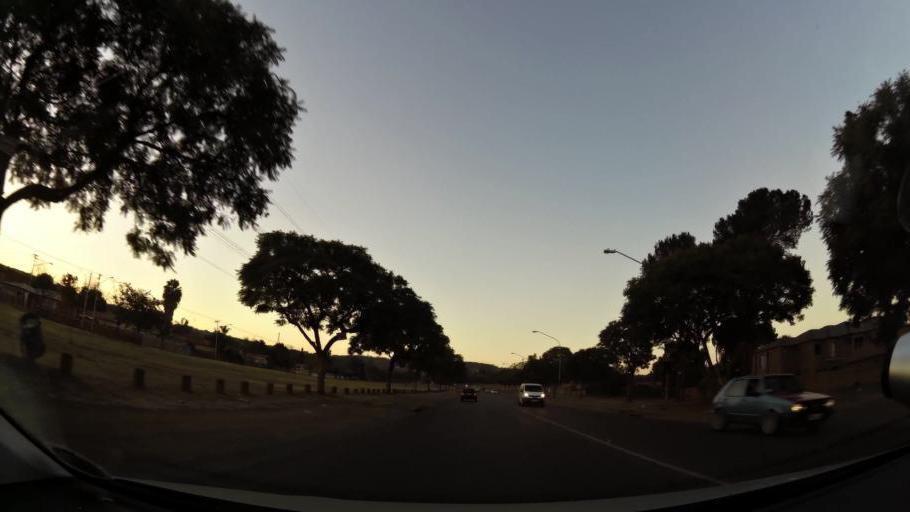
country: ZA
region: Gauteng
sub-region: City of Tshwane Metropolitan Municipality
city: Pretoria
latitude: -25.7392
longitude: 28.1361
